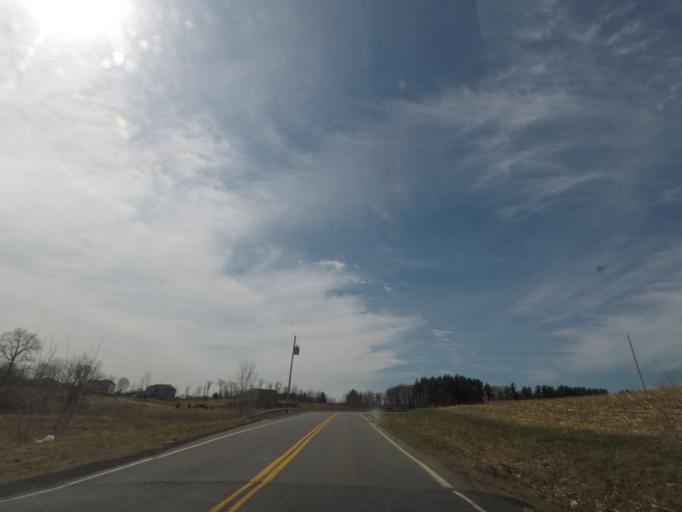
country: US
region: New York
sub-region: Saratoga County
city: Mechanicville
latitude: 42.9025
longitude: -73.7374
